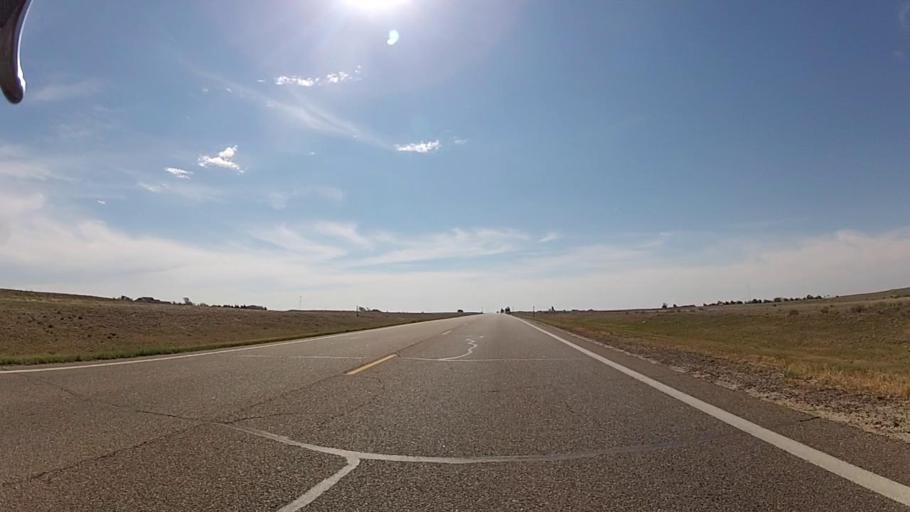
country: US
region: Kansas
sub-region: Grant County
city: Ulysses
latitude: 37.5687
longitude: -101.3245
